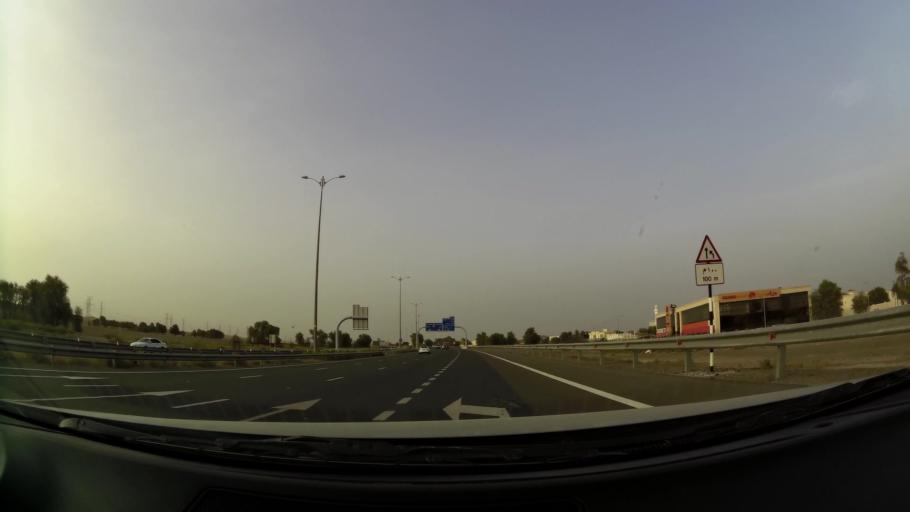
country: OM
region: Al Buraimi
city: Al Buraymi
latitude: 24.2802
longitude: 55.7302
